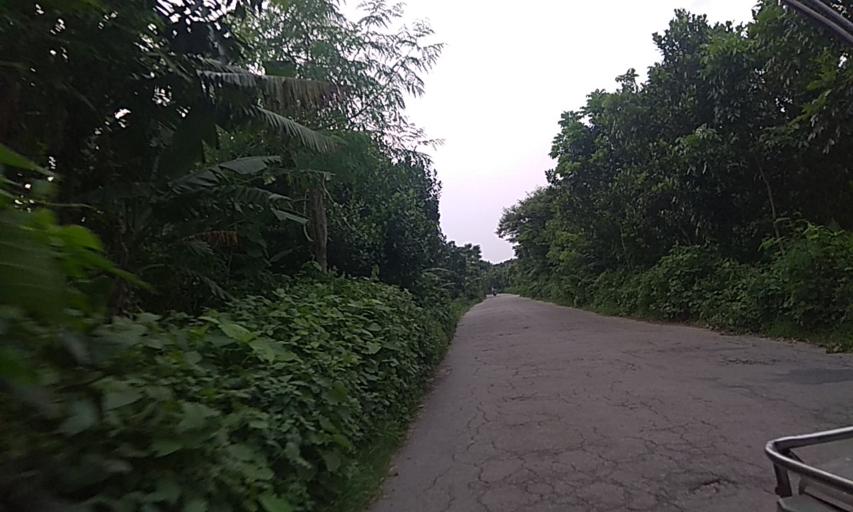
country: BD
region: Dhaka
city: Dohar
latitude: 23.4581
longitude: 89.9999
